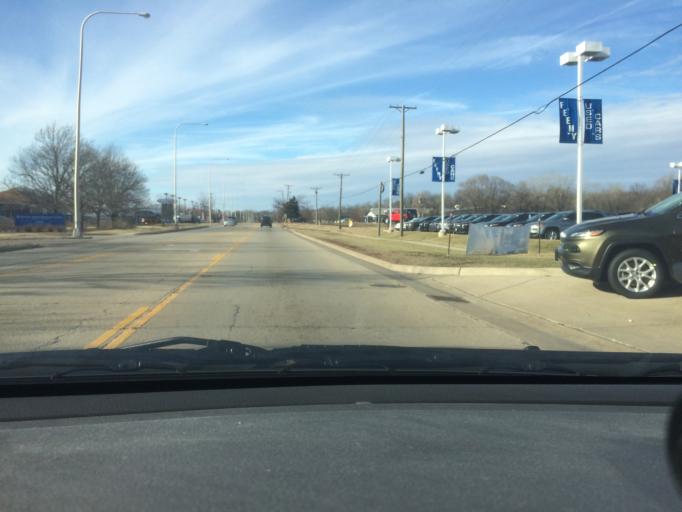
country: US
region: Illinois
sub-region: Kane County
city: Elgin
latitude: 42.0333
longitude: -88.2522
